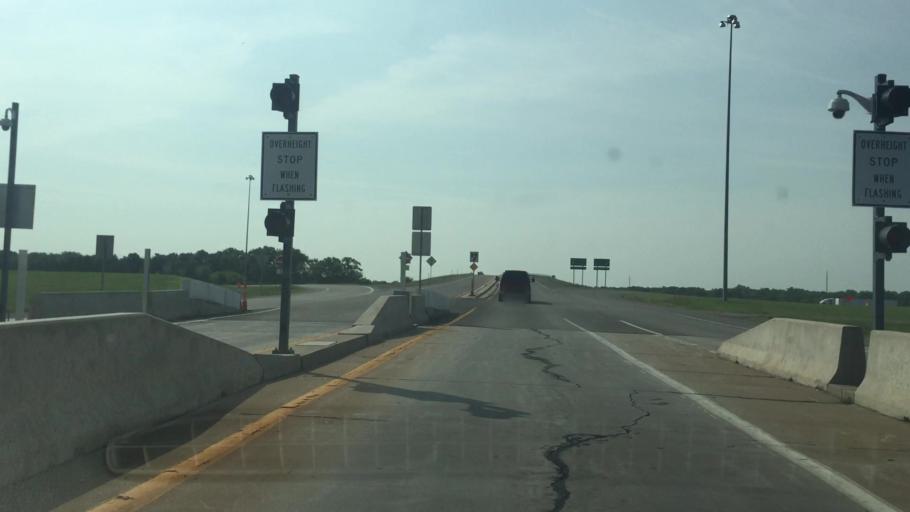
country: US
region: Kansas
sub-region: Butler County
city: Andover
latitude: 37.6887
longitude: -97.1824
